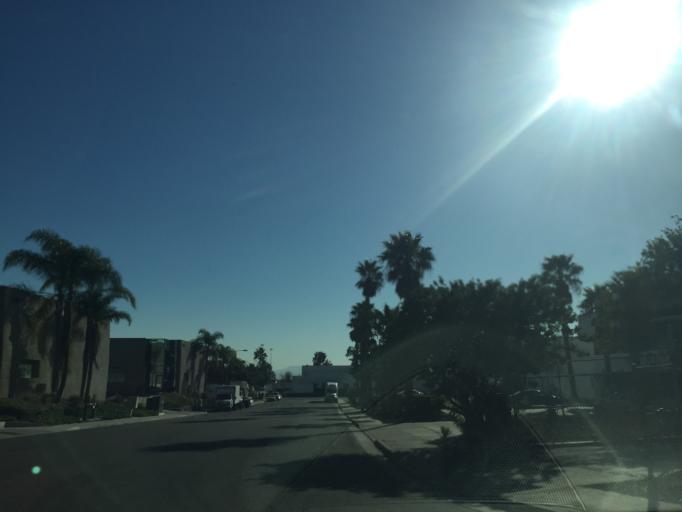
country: MX
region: Baja California
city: Tijuana
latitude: 32.5560
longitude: -116.9342
